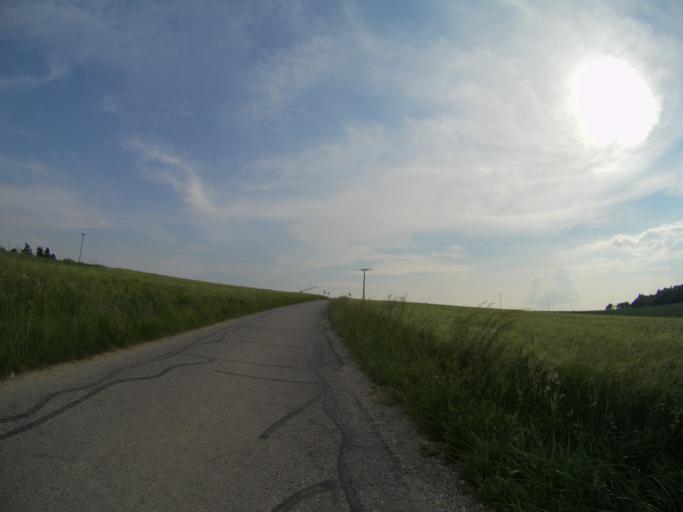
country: DE
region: Bavaria
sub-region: Upper Bavaria
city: Marzling
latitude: 48.4259
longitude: 11.7785
